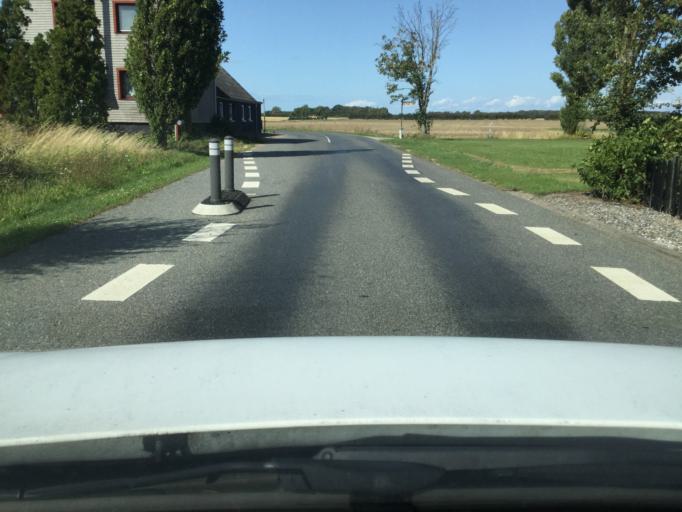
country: DK
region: Zealand
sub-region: Lolland Kommune
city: Rodby
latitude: 54.7113
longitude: 11.3844
